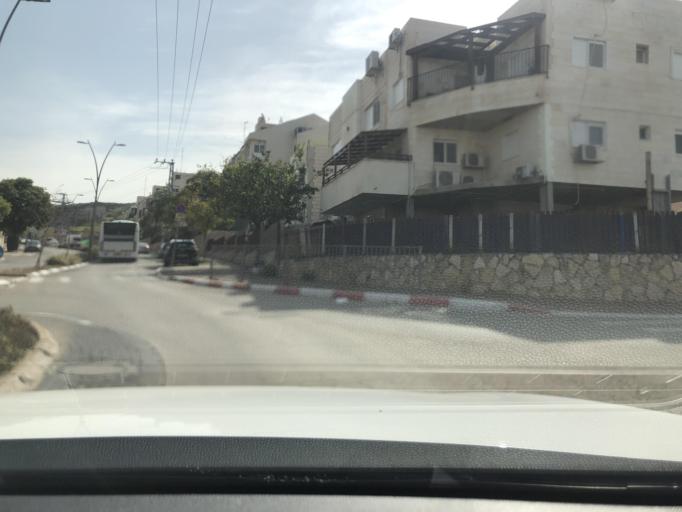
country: IL
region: Central District
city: Rosh Ha'Ayin
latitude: 32.0867
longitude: 34.9557
